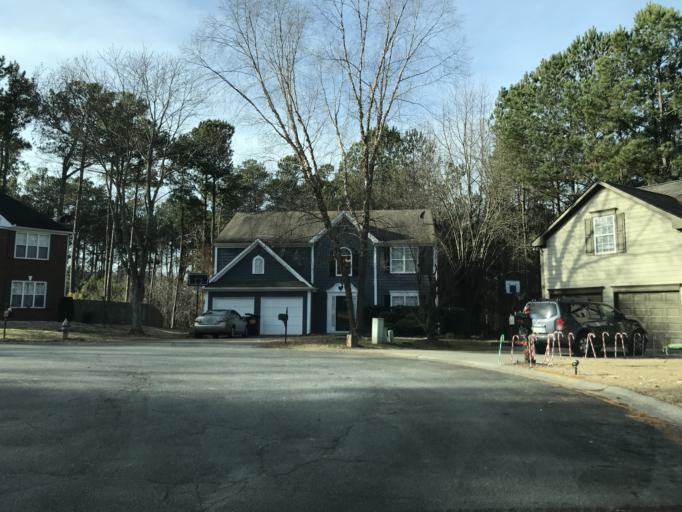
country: US
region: Georgia
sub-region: Cobb County
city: Kennesaw
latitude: 34.0577
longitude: -84.5960
